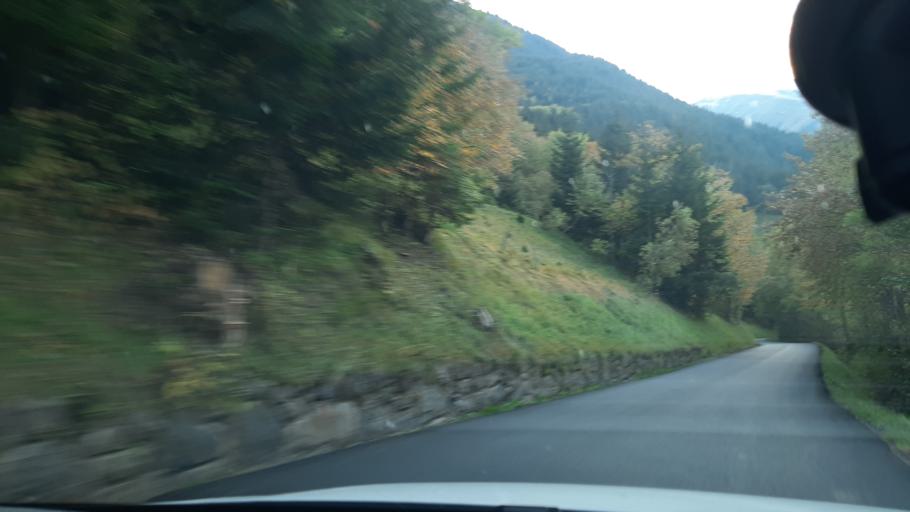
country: FR
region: Rhone-Alpes
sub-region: Departement de la Savoie
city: Saint-Jean-de-Maurienne
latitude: 45.1988
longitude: 6.3064
